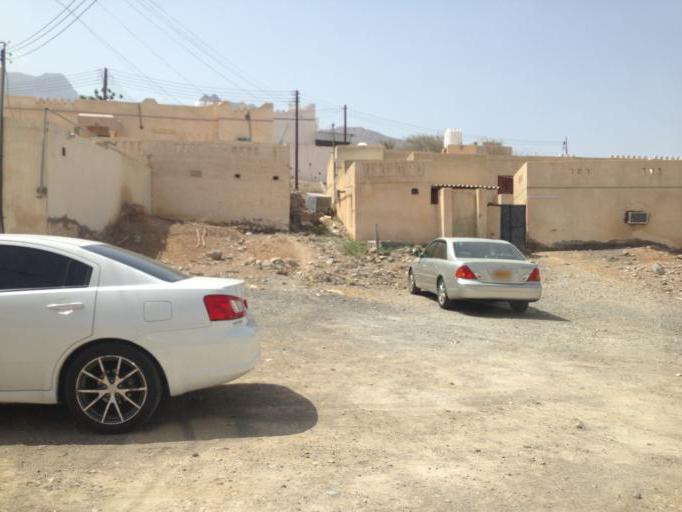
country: OM
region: Ash Sharqiyah
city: Ibra'
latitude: 23.0888
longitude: 58.8548
